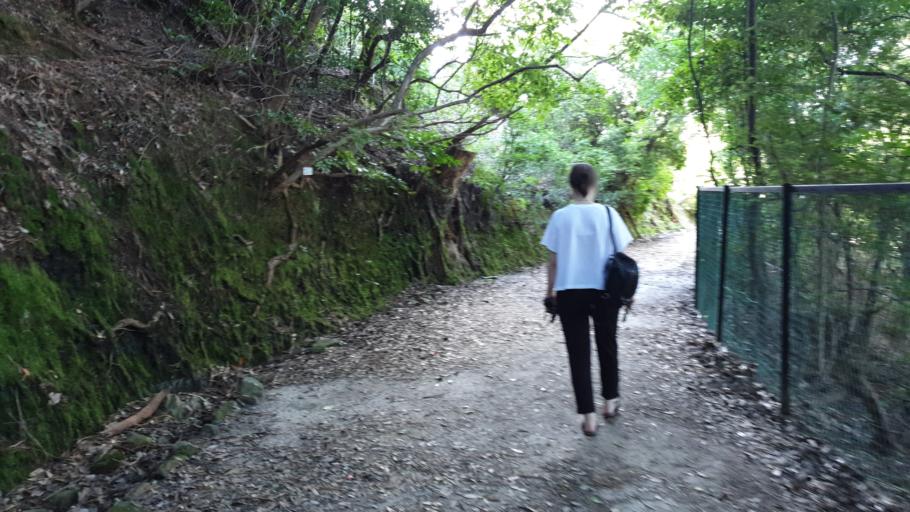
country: JP
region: Hiroshima
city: Miyajima
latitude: 34.2939
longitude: 132.3182
